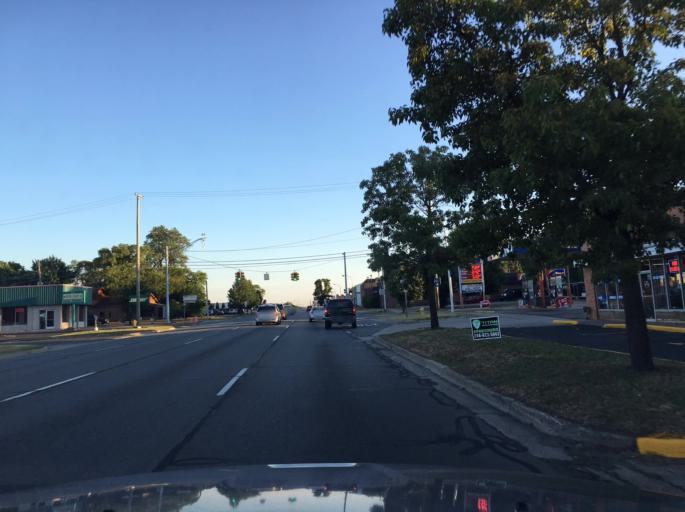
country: US
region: Michigan
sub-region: Macomb County
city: Mount Clemens
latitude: 42.5827
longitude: -82.8850
